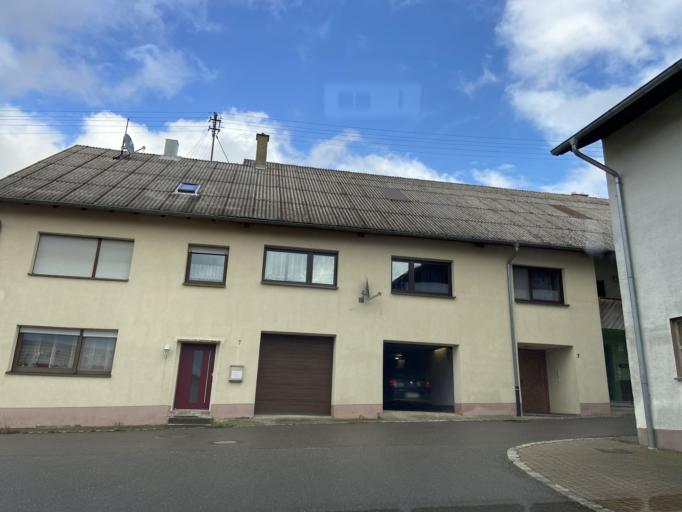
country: DE
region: Baden-Wuerttemberg
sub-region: Tuebingen Region
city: Leibertingen
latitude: 48.0578
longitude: 9.0297
